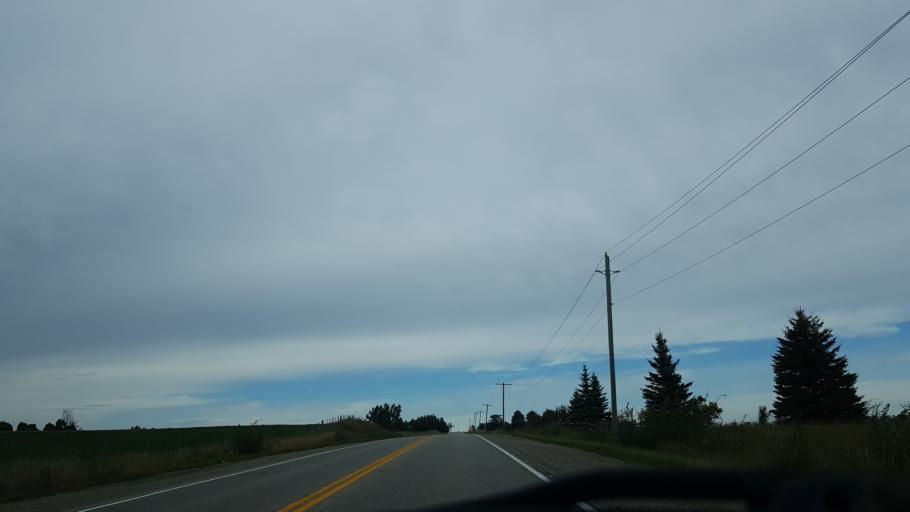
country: CA
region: Ontario
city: Shelburne
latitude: 44.1290
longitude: -80.0284
